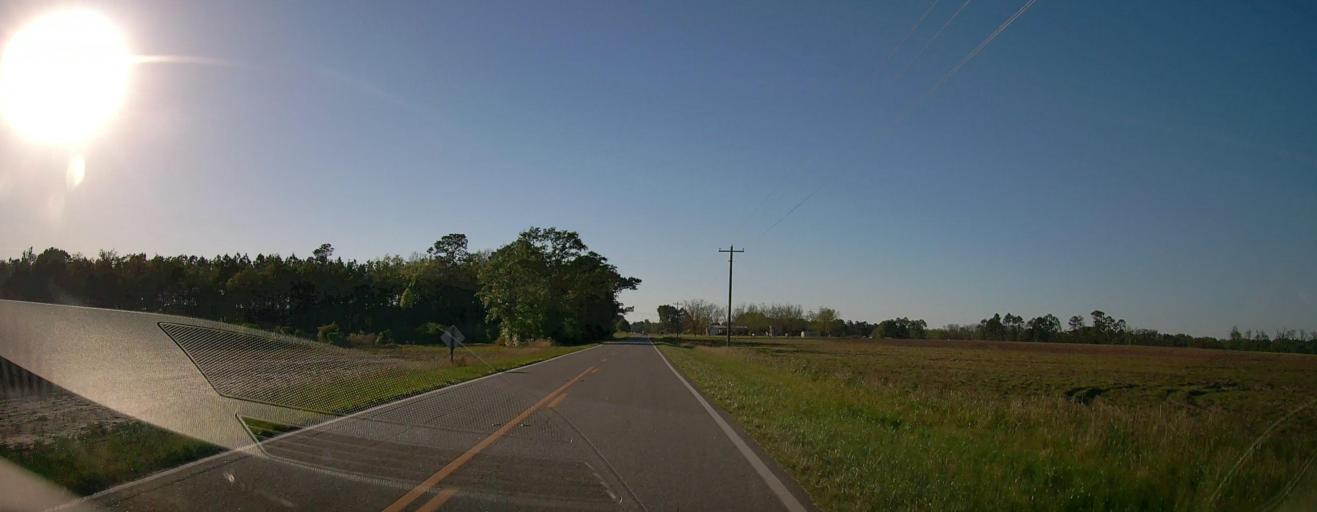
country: US
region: Georgia
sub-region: Ben Hill County
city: Fitzgerald
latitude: 31.6611
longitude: -83.1784
